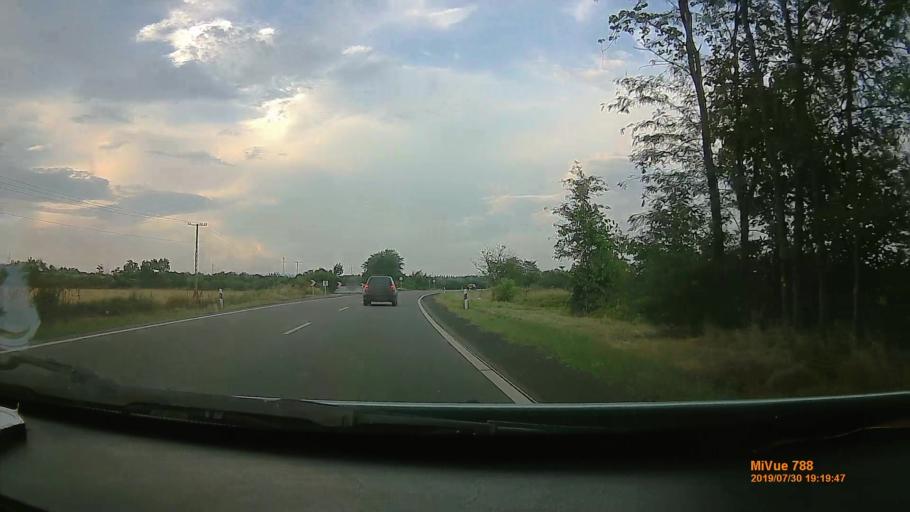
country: HU
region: Heves
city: Nagyrede
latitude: 47.7184
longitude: 19.8427
